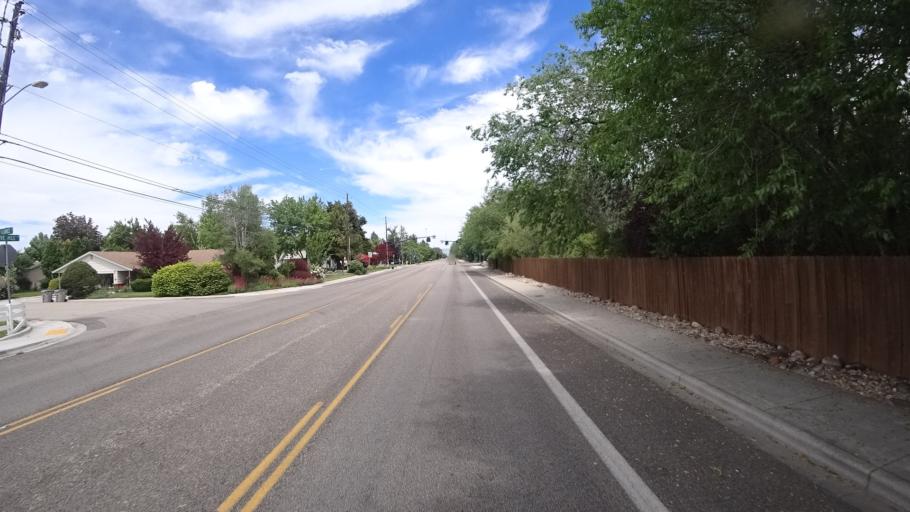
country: US
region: Idaho
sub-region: Ada County
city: Eagle
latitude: 43.6403
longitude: -116.3142
